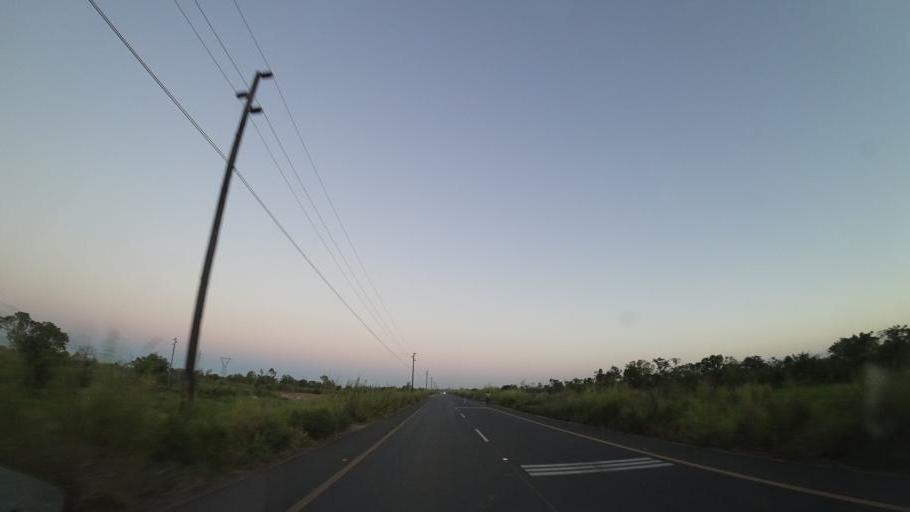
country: MZ
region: Sofala
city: Dondo
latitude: -19.5181
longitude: 34.6204
